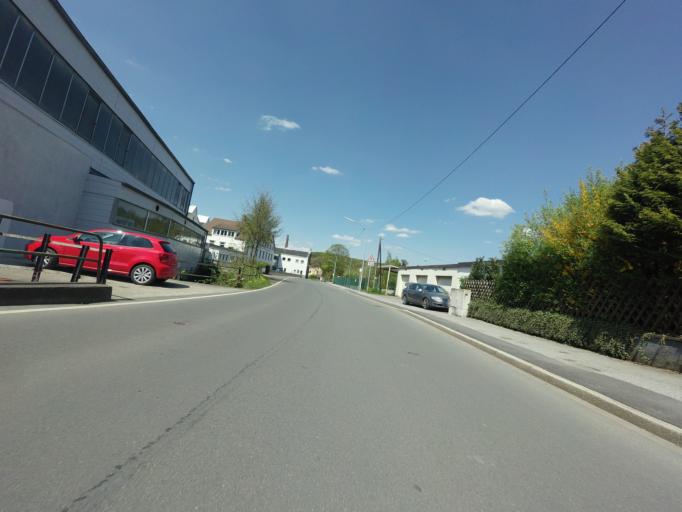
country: DE
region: North Rhine-Westphalia
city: Hemer
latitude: 51.3718
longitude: 7.7854
